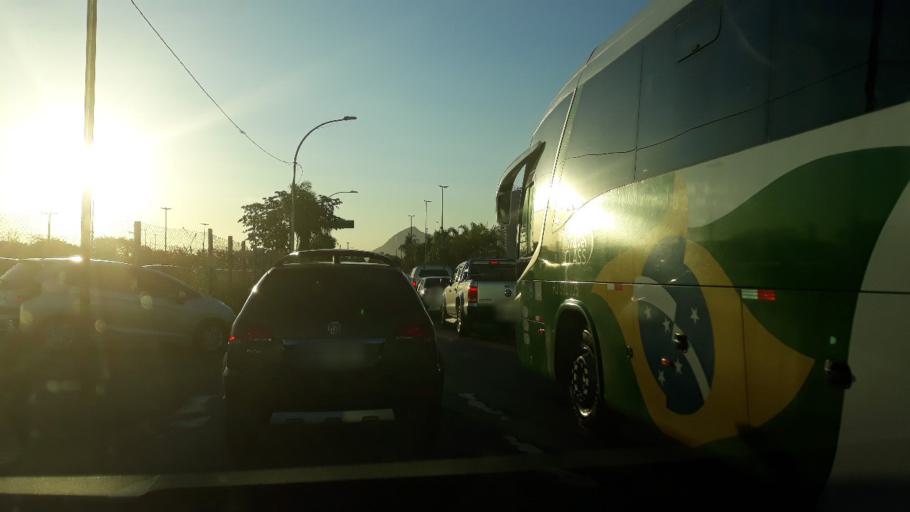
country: BR
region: Rio de Janeiro
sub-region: Rio De Janeiro
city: Rio de Janeiro
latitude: -22.9842
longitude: -43.3624
